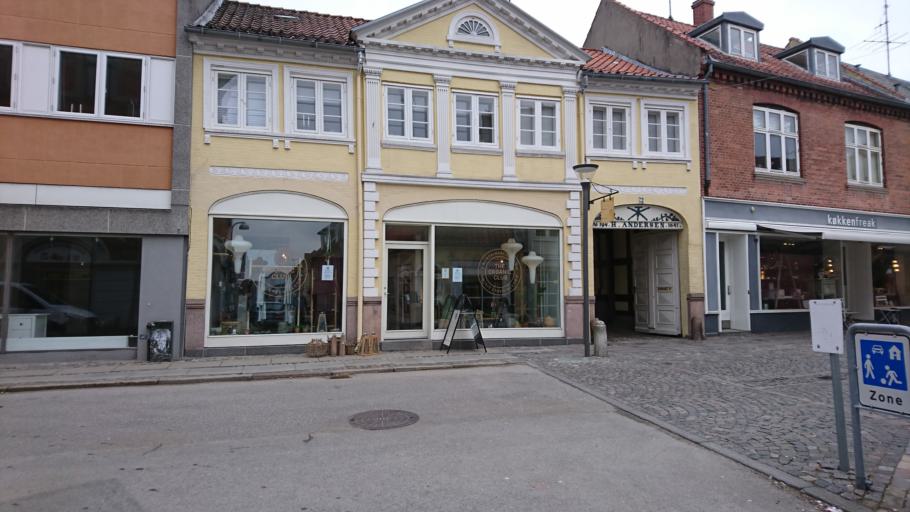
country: DK
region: South Denmark
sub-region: Svendborg Kommune
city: Svendborg
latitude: 55.0579
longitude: 10.6100
